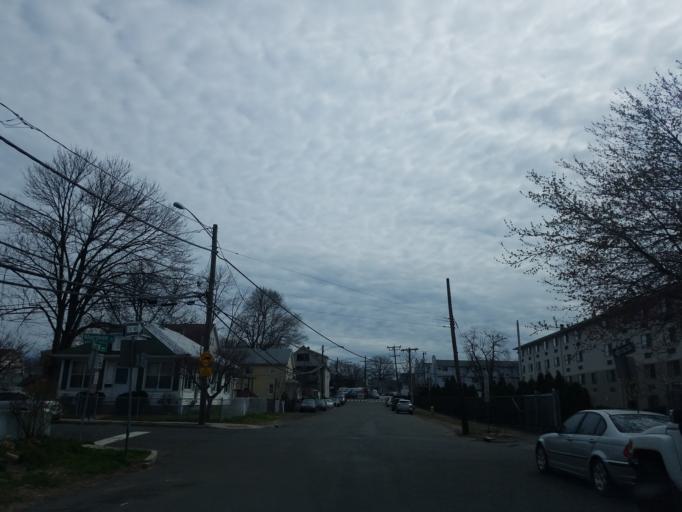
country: US
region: Connecticut
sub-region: Fairfield County
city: Riverside
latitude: 41.0461
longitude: -73.5598
